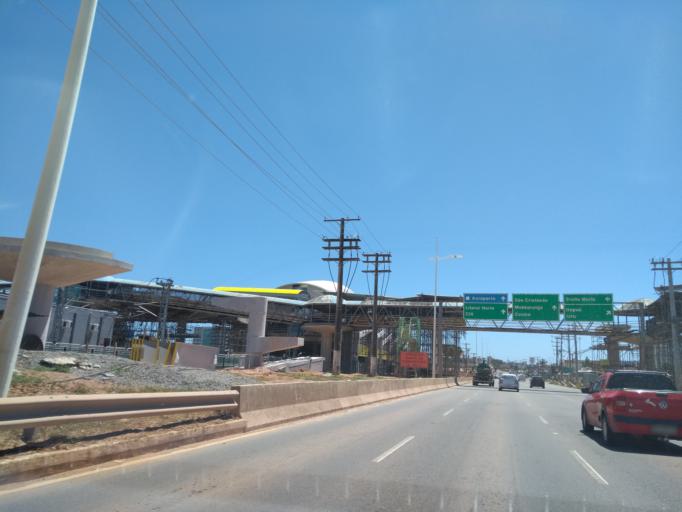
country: BR
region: Bahia
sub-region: Lauro De Freitas
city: Lauro de Freitas
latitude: -12.9221
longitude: -38.3604
